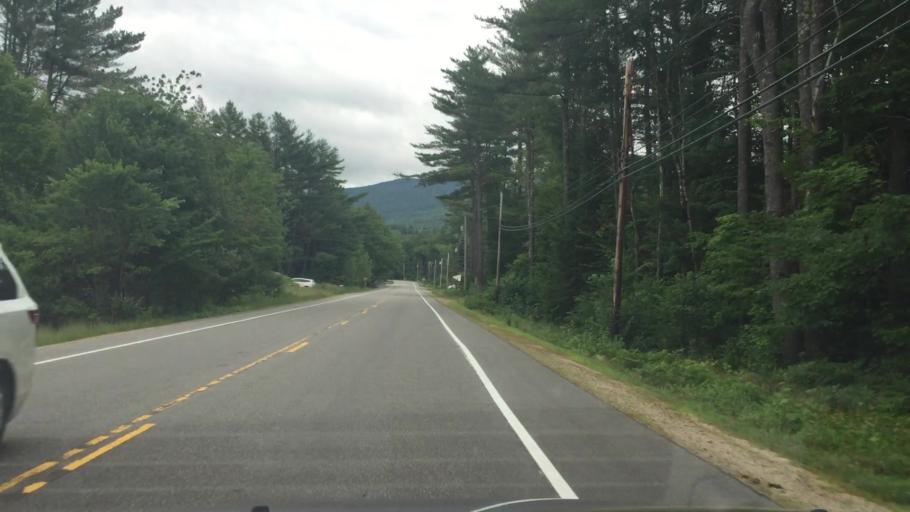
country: US
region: New Hampshire
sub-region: Carroll County
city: Tamworth
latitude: 43.8261
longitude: -71.3170
